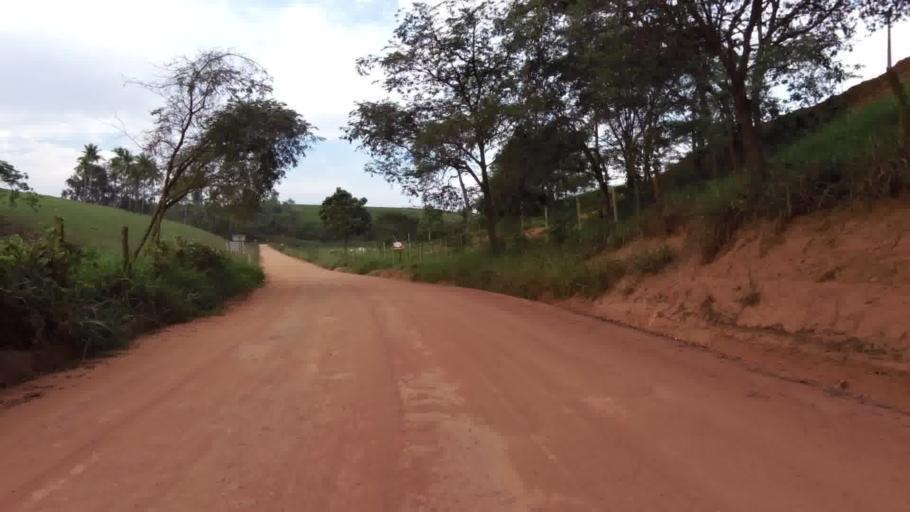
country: BR
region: Espirito Santo
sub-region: Piuma
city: Piuma
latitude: -20.8342
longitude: -40.7416
